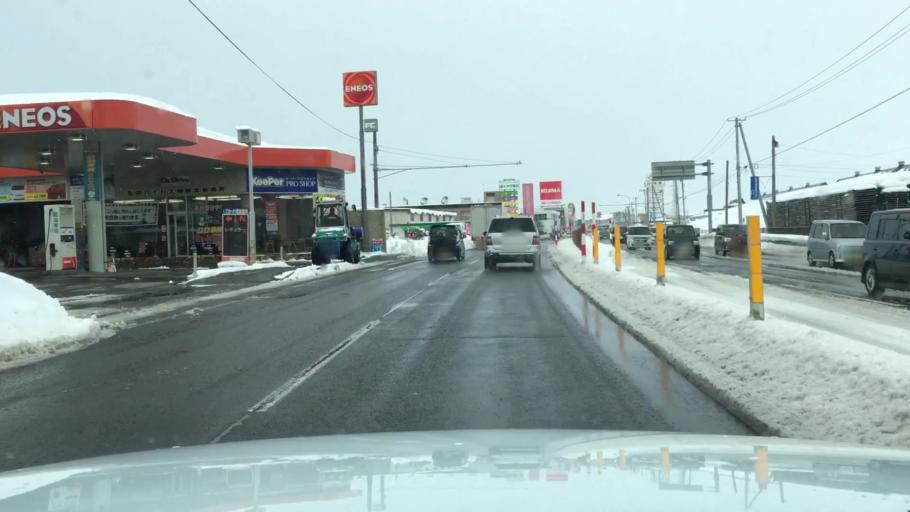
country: JP
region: Aomori
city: Hirosaki
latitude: 40.6041
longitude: 140.4991
